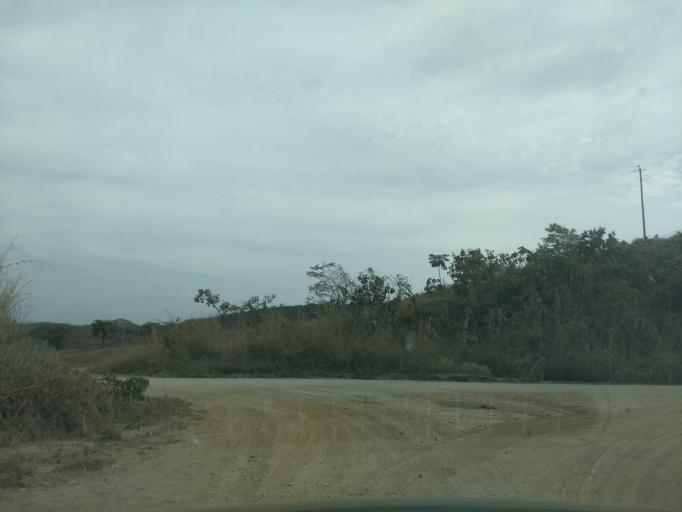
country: BR
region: Federal District
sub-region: Brasilia
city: Brasilia
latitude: -15.4822
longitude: -48.0642
